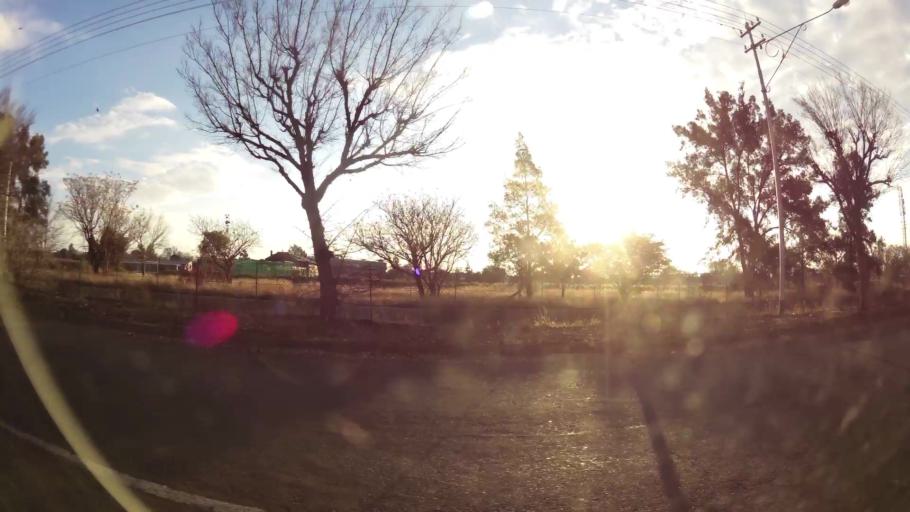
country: ZA
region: Orange Free State
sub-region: Mangaung Metropolitan Municipality
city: Bloemfontein
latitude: -29.1352
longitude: 26.1907
